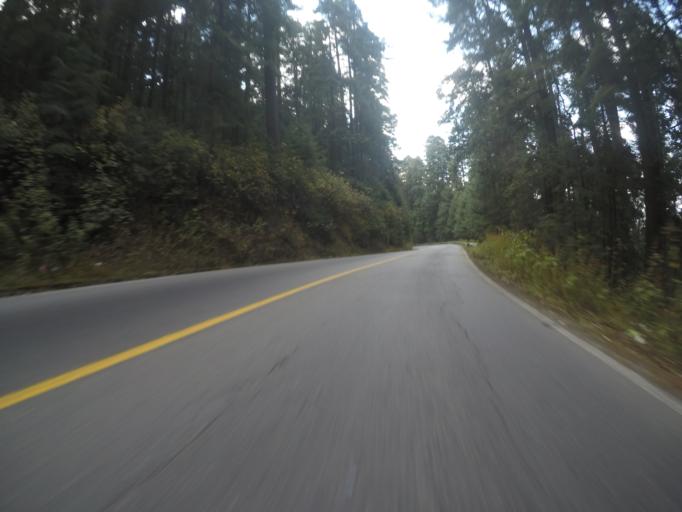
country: MX
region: Mexico
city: Cerro La Calera
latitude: 19.1834
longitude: -99.8047
